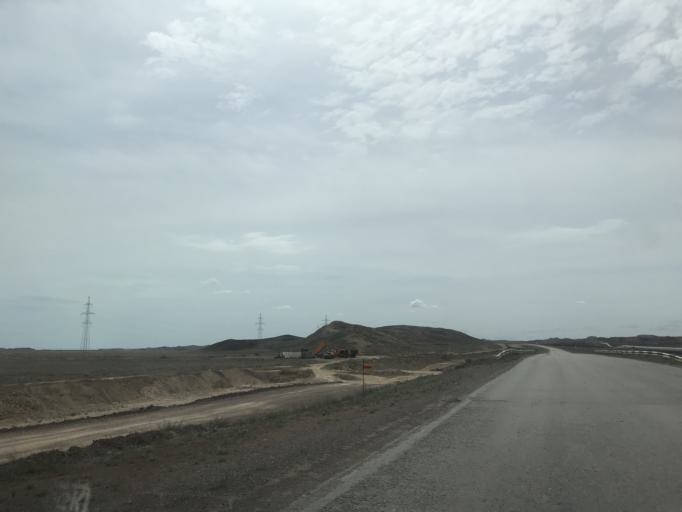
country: KZ
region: Zhambyl
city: Mynaral
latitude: 45.3751
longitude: 73.6557
